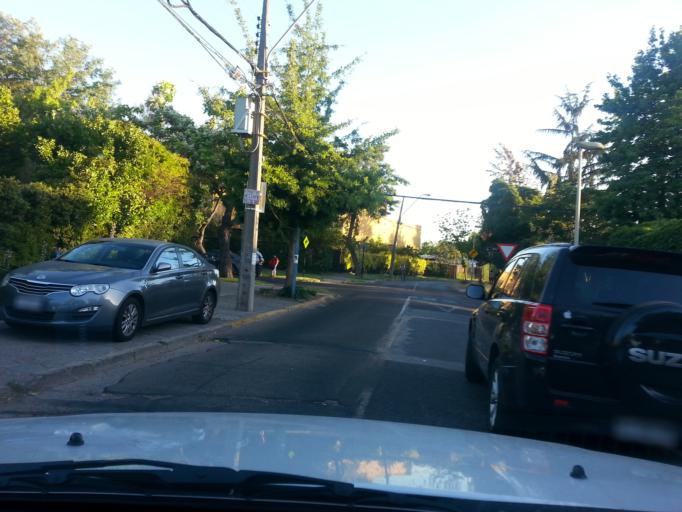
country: CL
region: Santiago Metropolitan
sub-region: Provincia de Santiago
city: Villa Presidente Frei, Nunoa, Santiago, Chile
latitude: -33.4239
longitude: -70.5565
